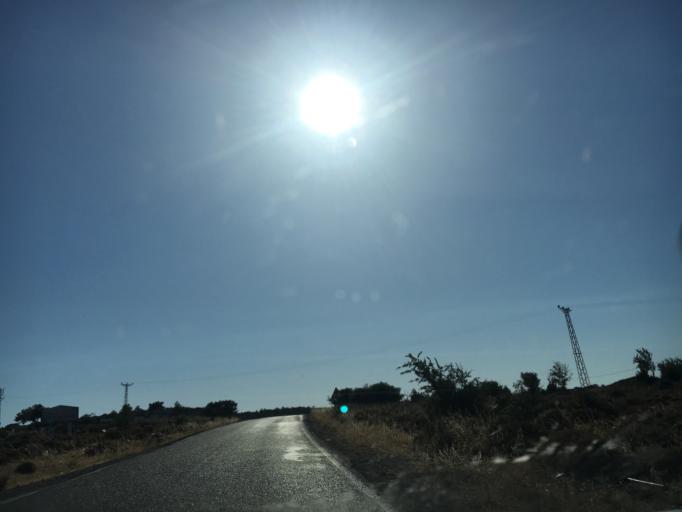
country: TR
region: Canakkale
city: Behram
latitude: 39.4974
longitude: 26.3556
